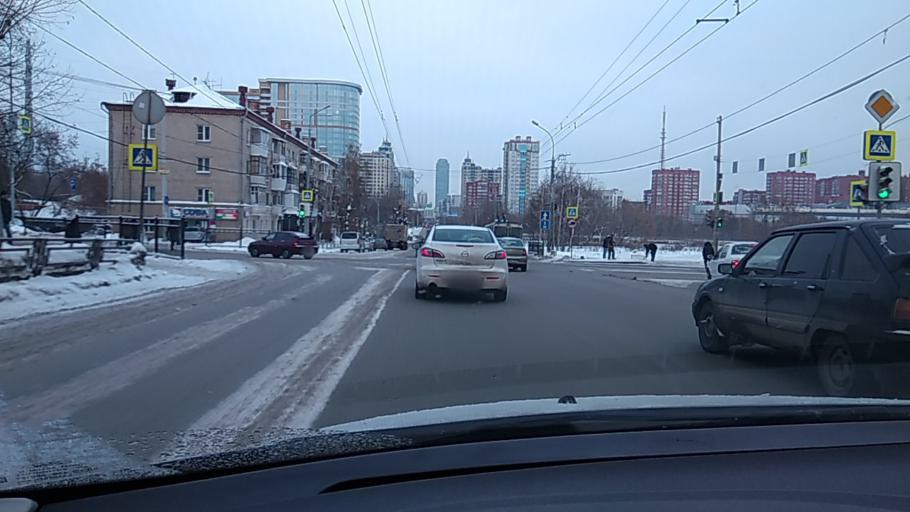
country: RU
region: Sverdlovsk
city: Yekaterinburg
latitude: 56.8164
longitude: 60.6207
